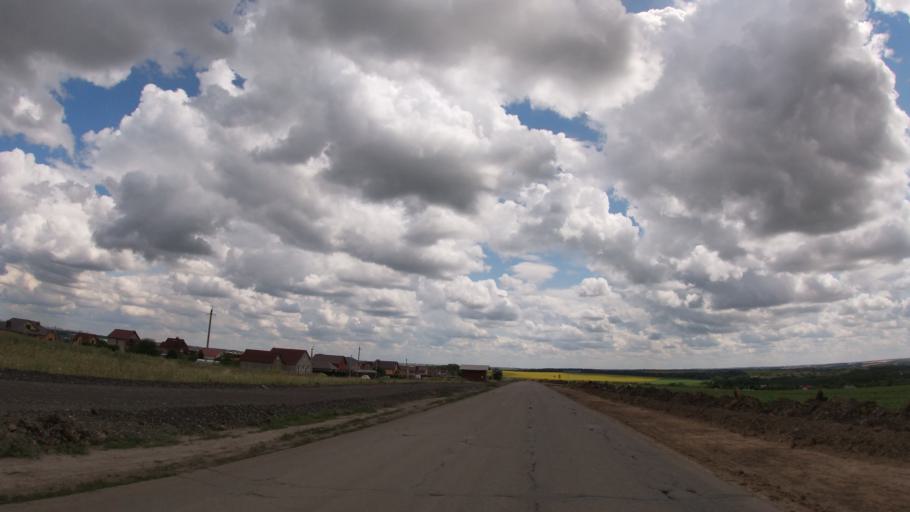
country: RU
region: Belgorod
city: Mayskiy
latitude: 50.5023
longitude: 36.4437
